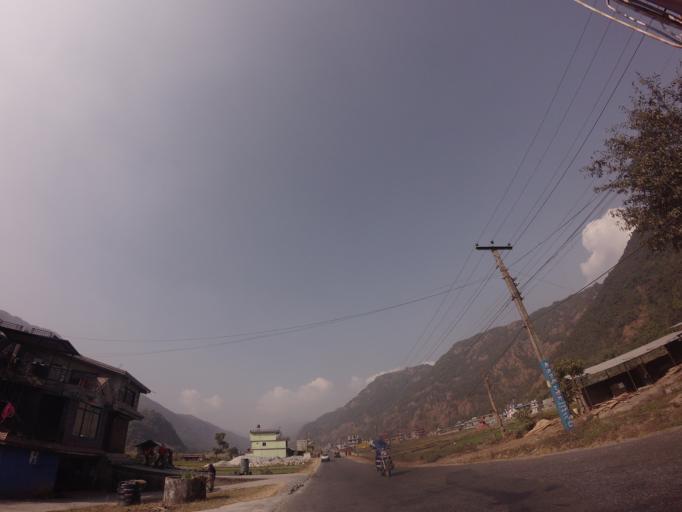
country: NP
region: Western Region
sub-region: Gandaki Zone
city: Pokhara
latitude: 28.2820
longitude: 83.9258
